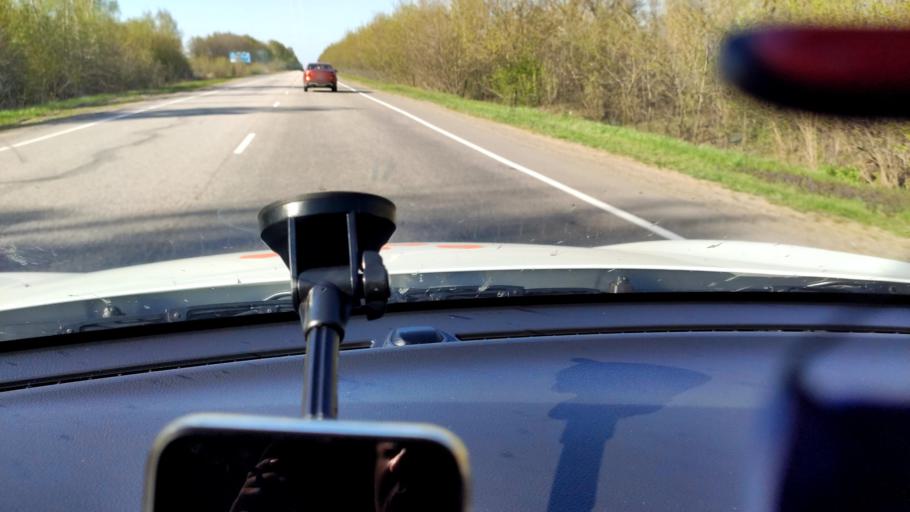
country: RU
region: Voronezj
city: Kolodeznyy
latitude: 51.3505
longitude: 39.0238
